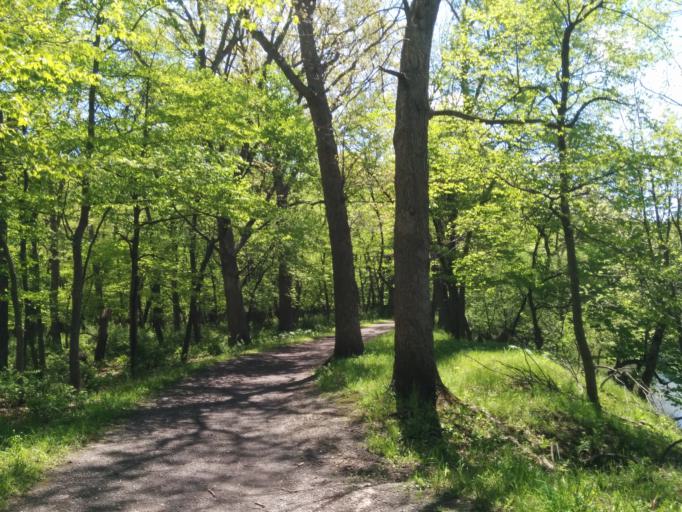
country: US
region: Illinois
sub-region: Cook County
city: Schiller Park
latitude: 41.9722
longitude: -87.8544
